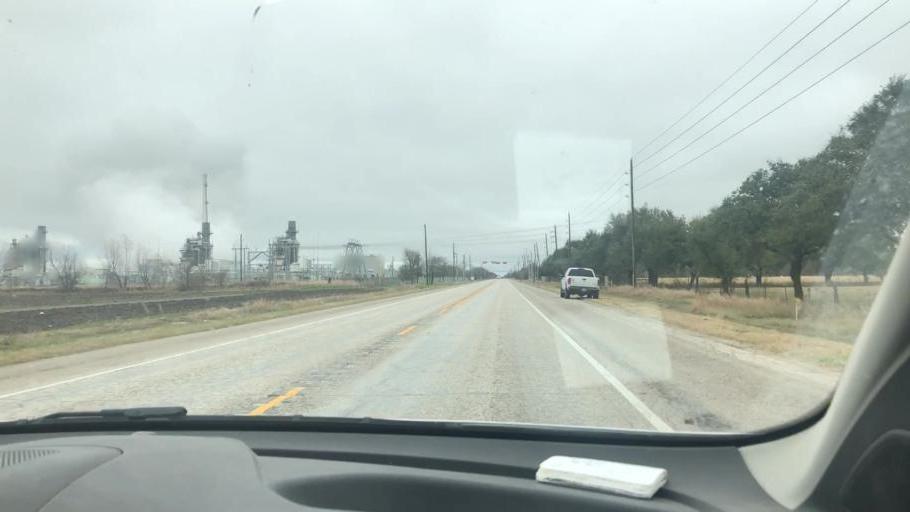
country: US
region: Texas
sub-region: Wharton County
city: Wharton
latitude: 29.2915
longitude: -96.0729
